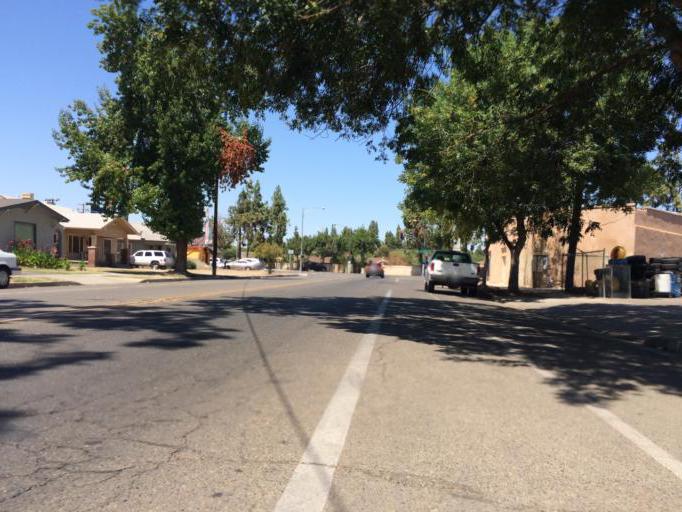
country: US
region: California
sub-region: Fresno County
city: Fresno
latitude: 36.7353
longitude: -119.7749
